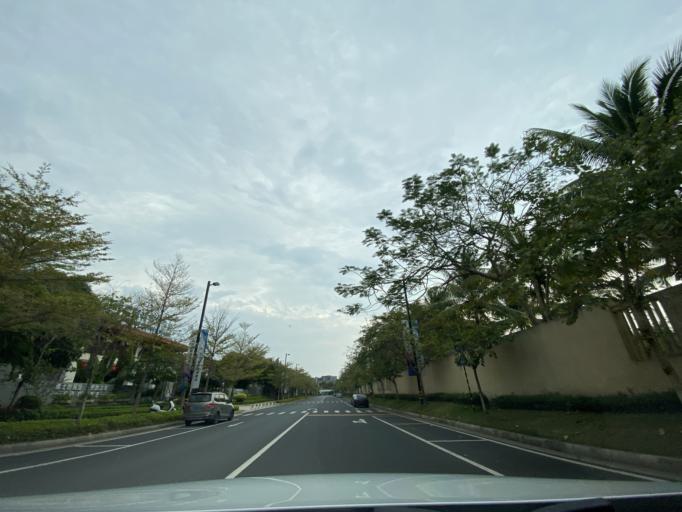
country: CN
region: Hainan
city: Yingzhou
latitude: 18.4042
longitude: 109.8550
